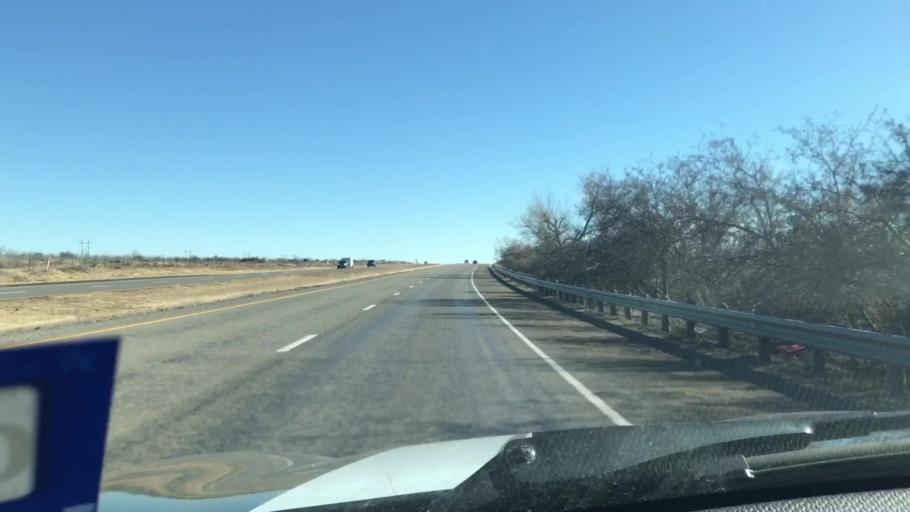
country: US
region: Texas
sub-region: Garza County
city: Post
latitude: 33.1062
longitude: -101.2648
